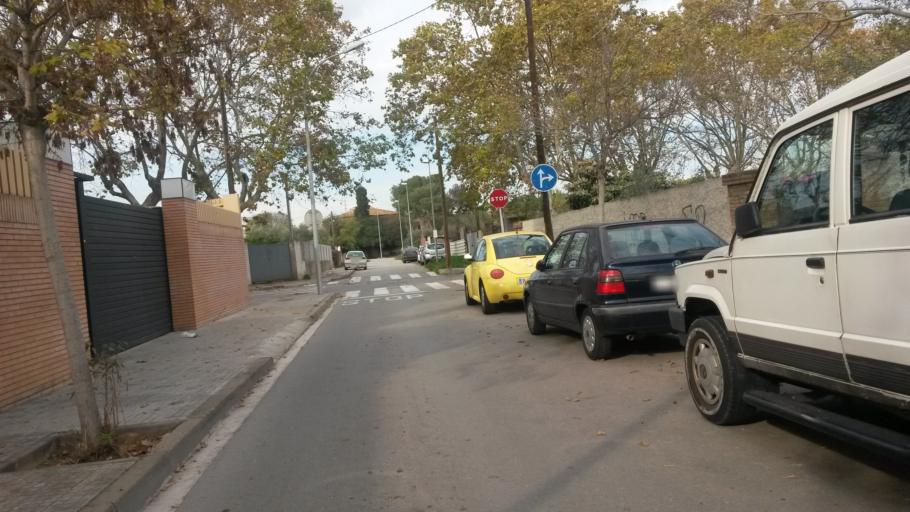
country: ES
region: Catalonia
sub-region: Provincia de Barcelona
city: Cerdanyola del Valles
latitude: 41.4966
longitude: 2.1353
